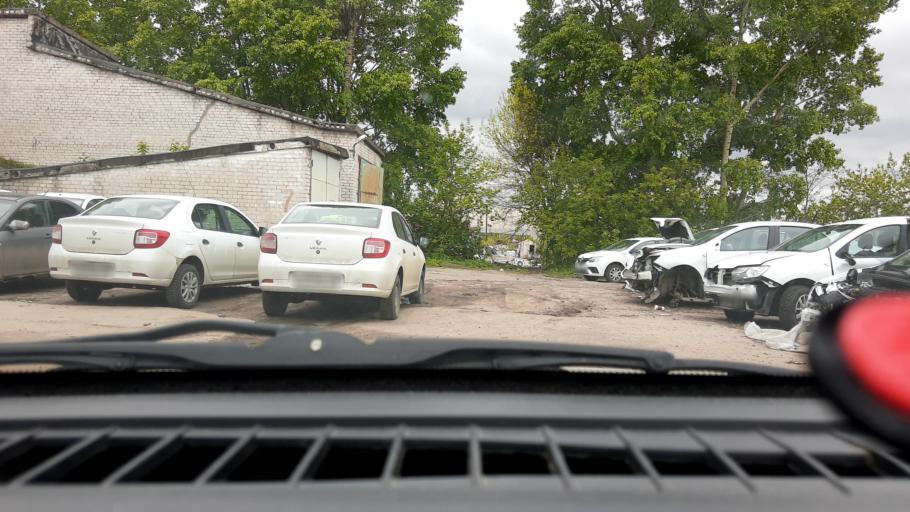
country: RU
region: Nizjnij Novgorod
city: Bor
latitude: 56.3092
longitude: 44.0606
